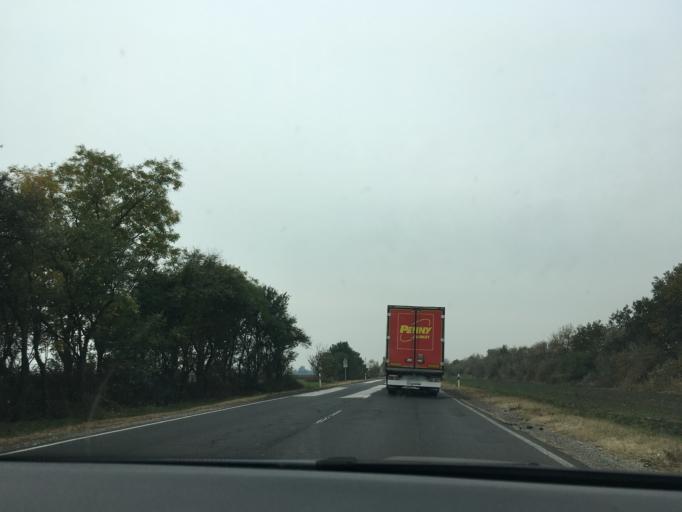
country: HU
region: Jasz-Nagykun-Szolnok
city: Fegyvernek
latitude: 47.2400
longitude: 20.5601
